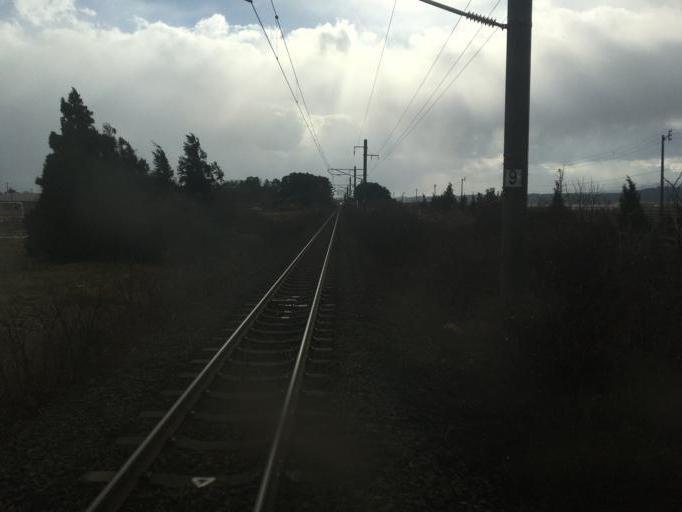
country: JP
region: Aomori
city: Aomori Shi
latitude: 40.9583
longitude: 140.6553
